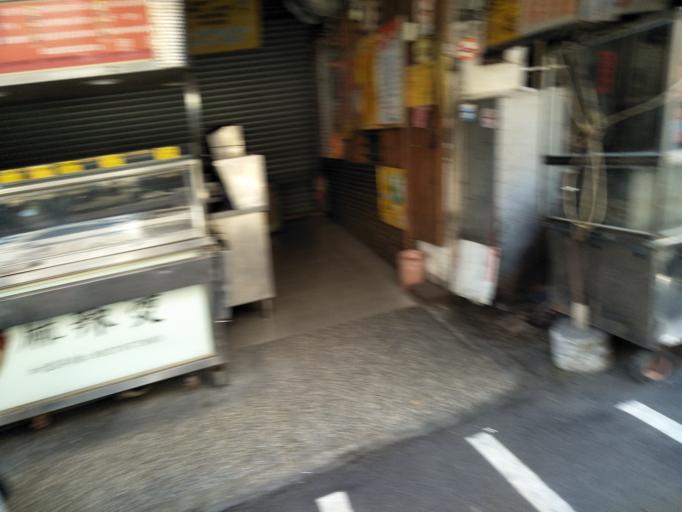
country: TW
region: Taiwan
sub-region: Changhua
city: Chang-hua
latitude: 24.0763
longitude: 120.5403
